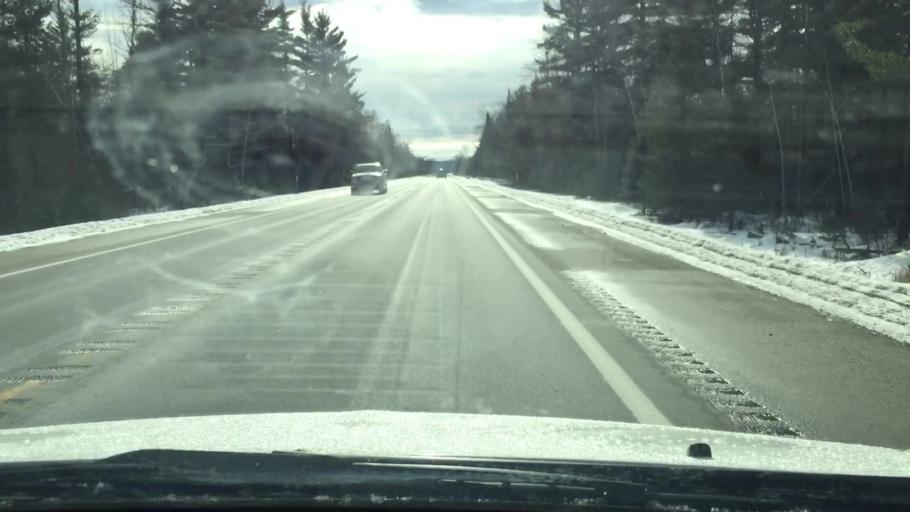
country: US
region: Michigan
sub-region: Kalkaska County
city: Kalkaska
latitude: 44.7122
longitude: -85.1938
